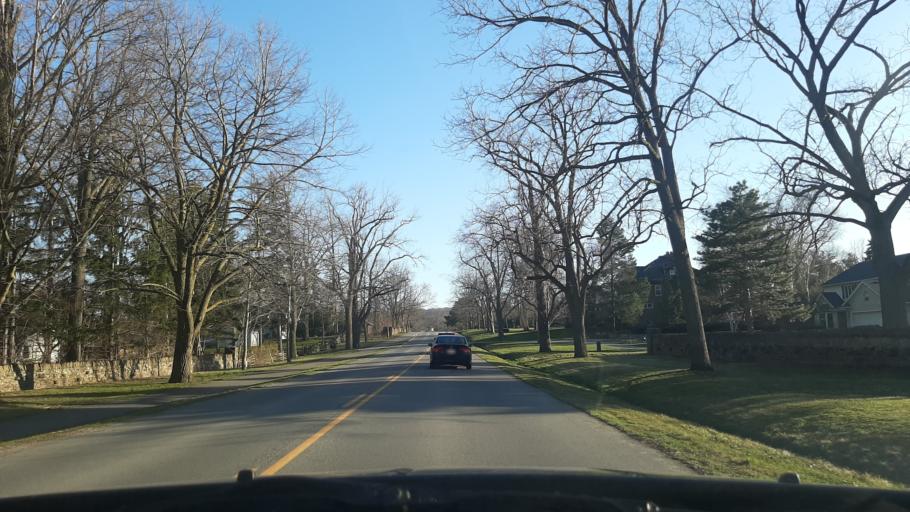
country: US
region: New York
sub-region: Niagara County
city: Lewiston
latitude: 43.1771
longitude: -79.0585
